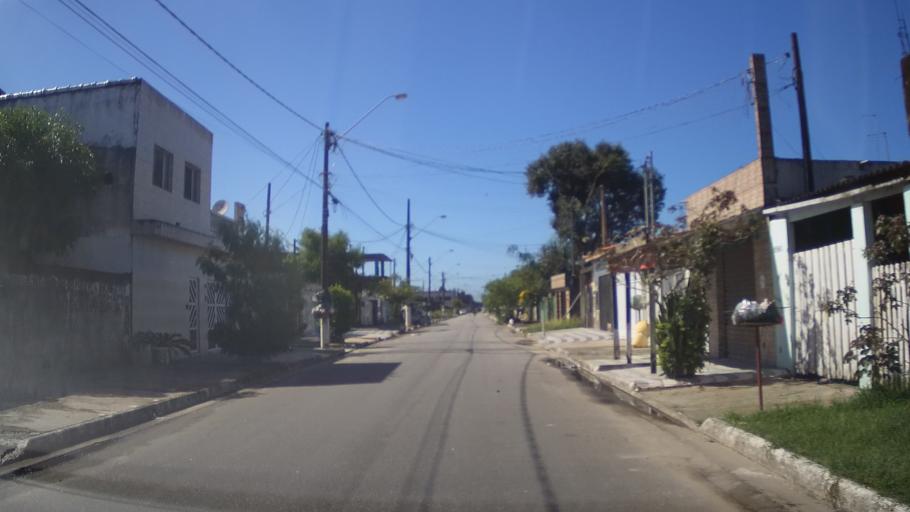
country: BR
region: Sao Paulo
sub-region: Mongagua
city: Mongagua
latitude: -24.0270
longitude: -46.5286
